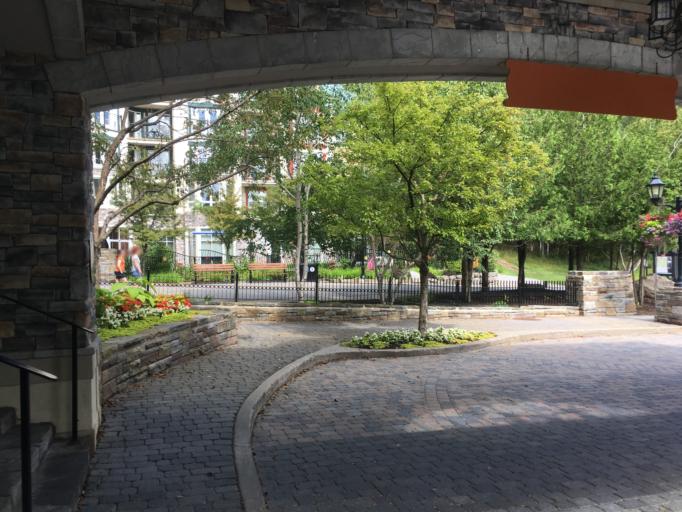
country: CA
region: Quebec
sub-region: Laurentides
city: Mont-Tremblant
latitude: 46.2123
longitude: -74.5833
